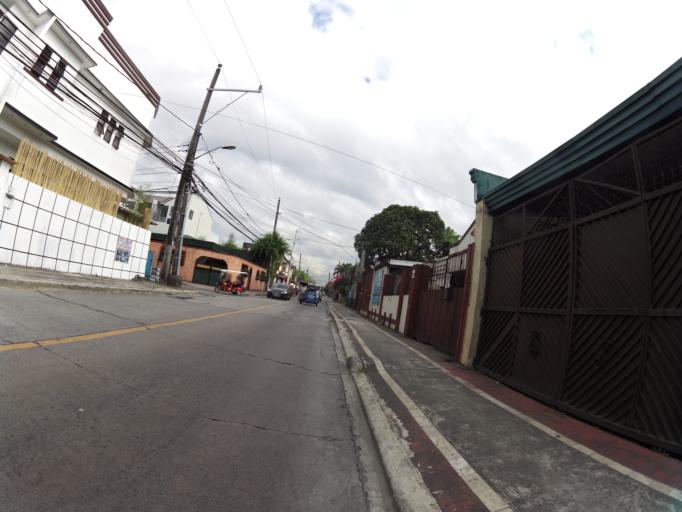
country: PH
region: Calabarzon
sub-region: Province of Rizal
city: Antipolo
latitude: 14.6415
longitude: 121.1087
